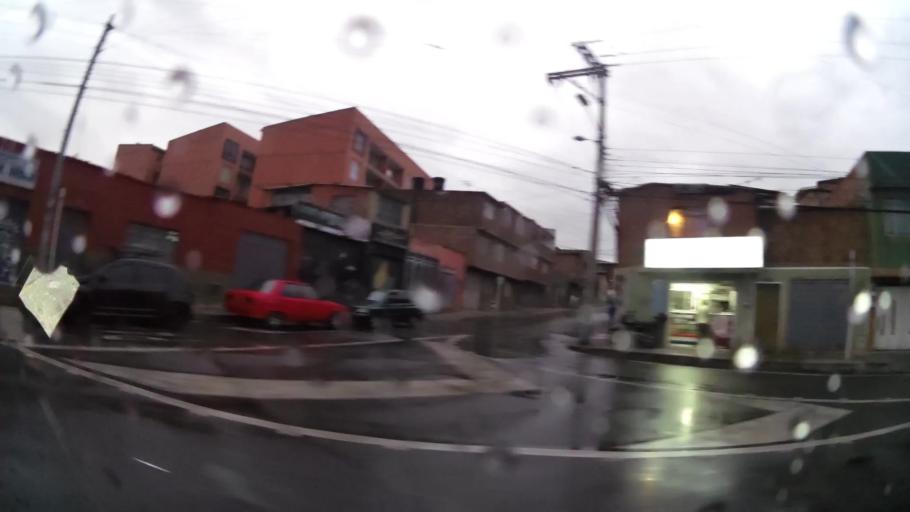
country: CO
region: Bogota D.C.
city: Bogota
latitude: 4.5849
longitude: -74.1373
